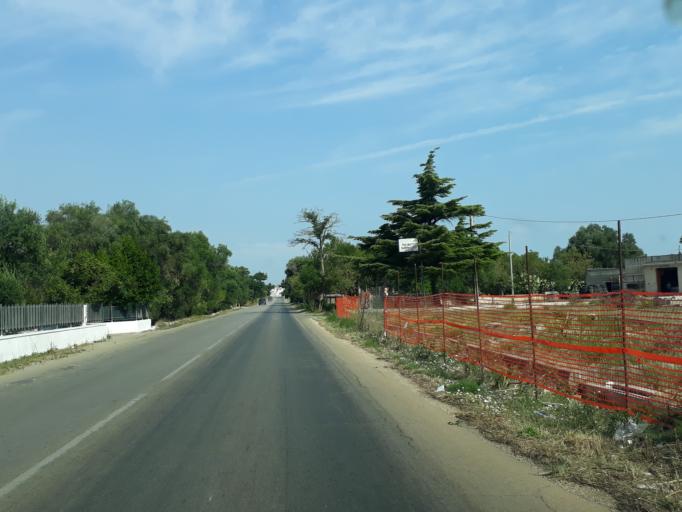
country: IT
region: Apulia
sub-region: Provincia di Brindisi
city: Carovigno
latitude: 40.6881
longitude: 17.6764
